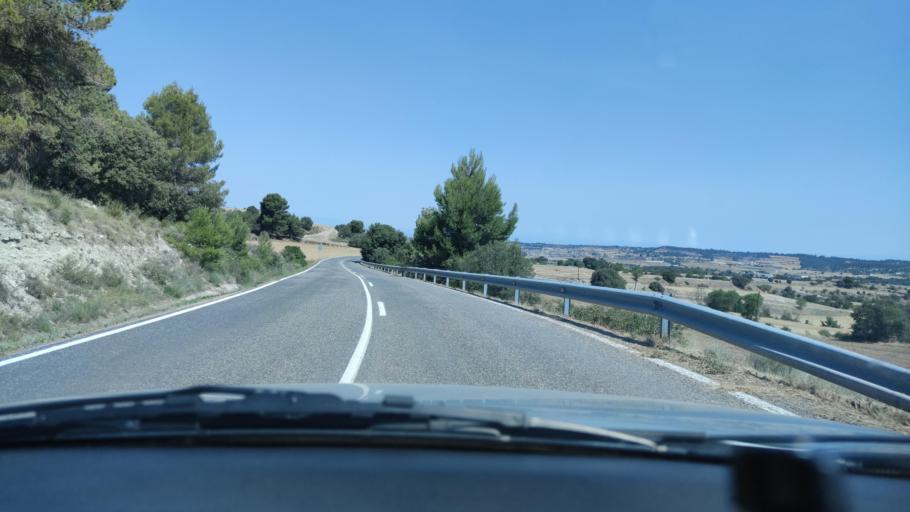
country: ES
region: Catalonia
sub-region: Provincia de Tarragona
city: Santa Coloma de Queralt
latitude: 41.6113
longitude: 1.3444
